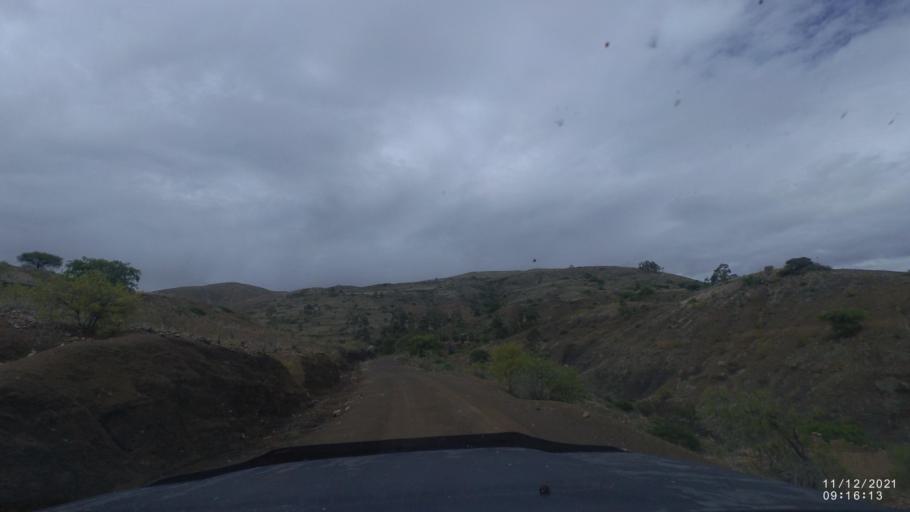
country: BO
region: Cochabamba
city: Tarata
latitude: -17.8824
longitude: -65.9626
